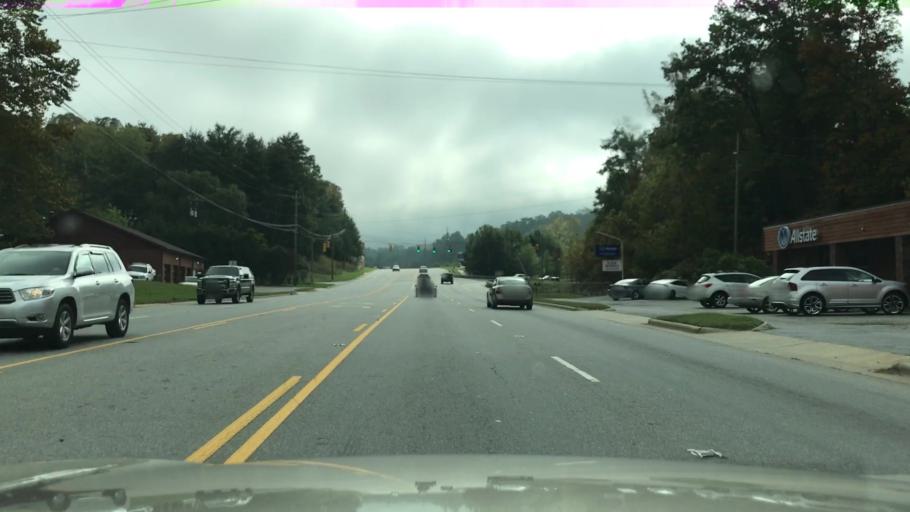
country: US
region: North Carolina
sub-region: Buncombe County
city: Biltmore Forest
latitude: 35.5559
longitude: -82.4836
